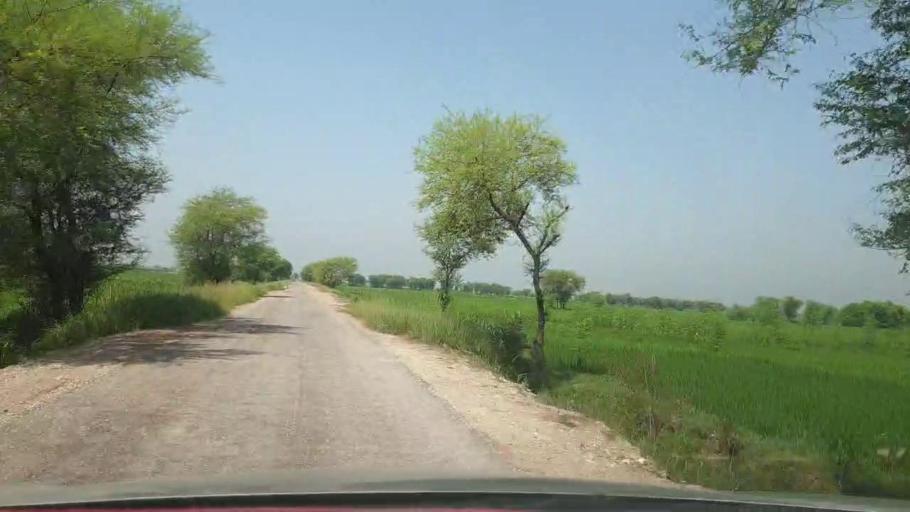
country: PK
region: Sindh
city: Kambar
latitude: 27.6113
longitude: 67.8795
